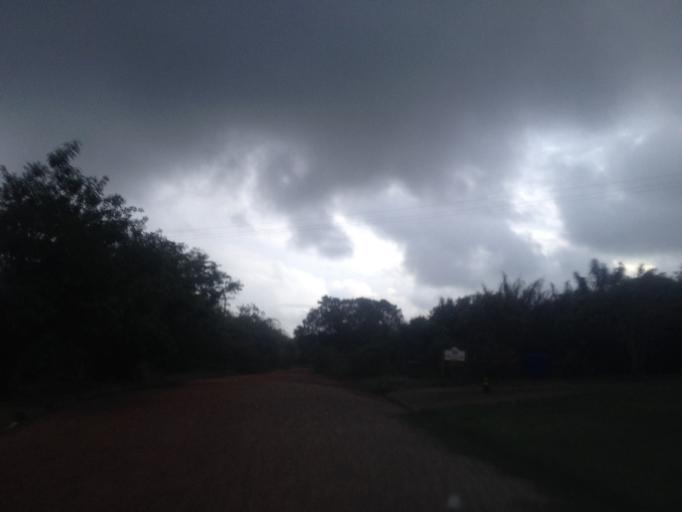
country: BR
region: Bahia
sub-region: Mata De Sao Joao
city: Mata de Sao Joao
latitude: -12.5696
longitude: -38.0218
